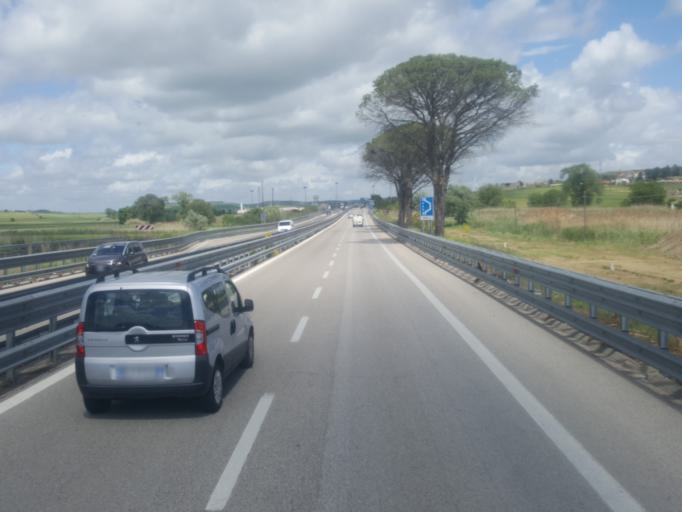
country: IT
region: Basilicate
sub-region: Provincia di Matera
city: Matera
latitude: 40.7129
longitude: 16.5799
